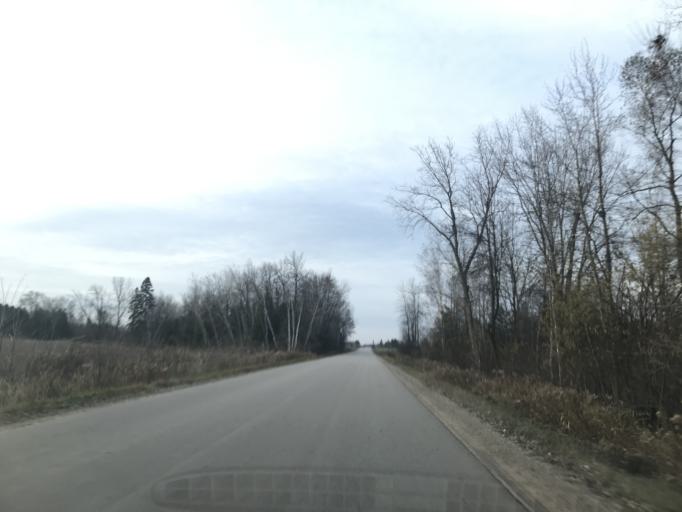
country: US
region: Wisconsin
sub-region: Marinette County
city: Peshtigo
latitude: 45.0880
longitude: -87.7995
